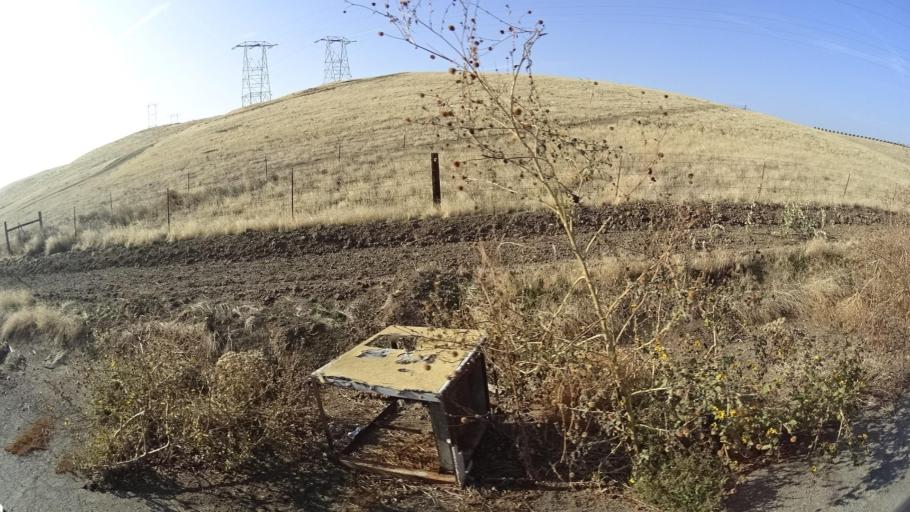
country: US
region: California
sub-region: Tulare County
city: Richgrove
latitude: 35.6392
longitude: -119.0420
